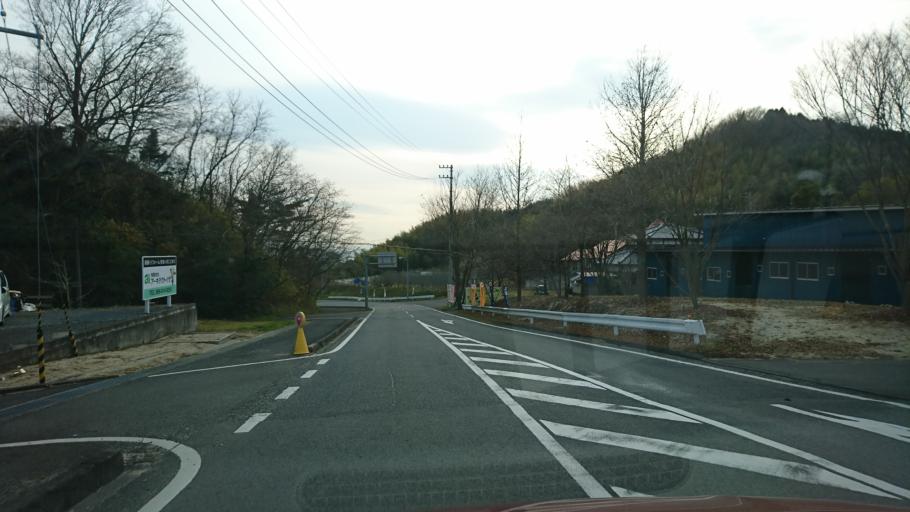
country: JP
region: Ehime
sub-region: Shikoku-chuo Shi
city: Matsuyama
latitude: 33.9015
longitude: 132.8074
